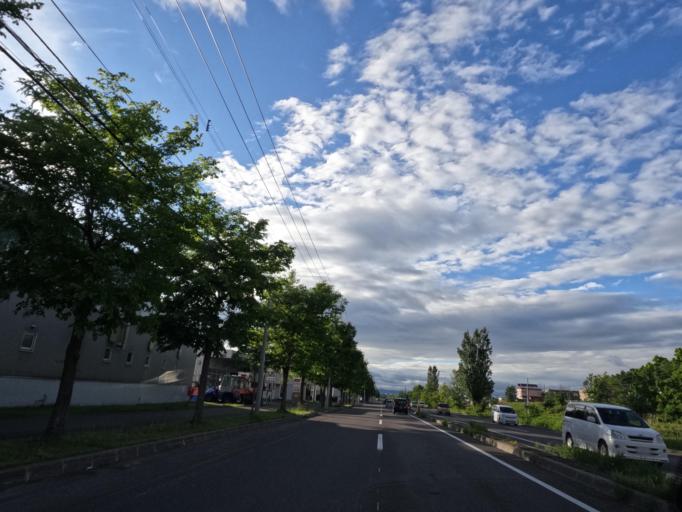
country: JP
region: Hokkaido
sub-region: Asahikawa-shi
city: Asahikawa
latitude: 43.7322
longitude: 142.3644
